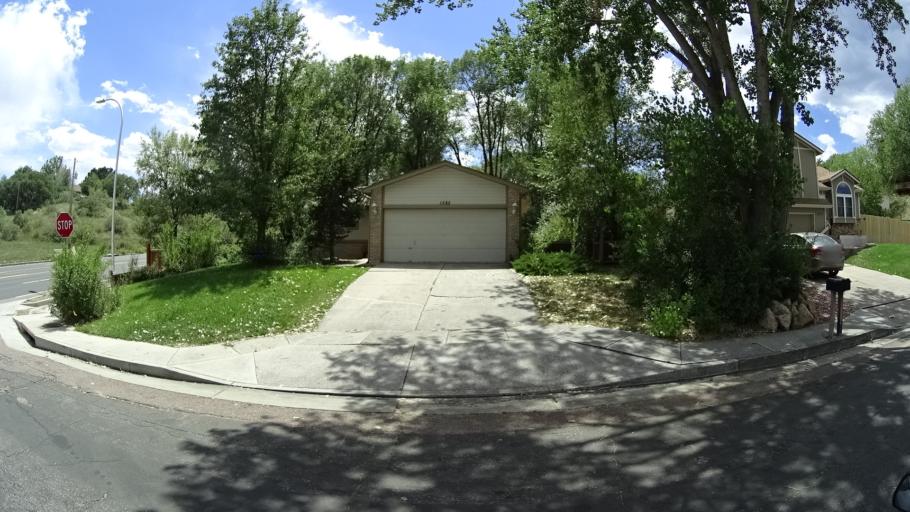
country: US
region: Colorado
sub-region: El Paso County
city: Stratmoor
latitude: 38.7854
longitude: -104.7976
